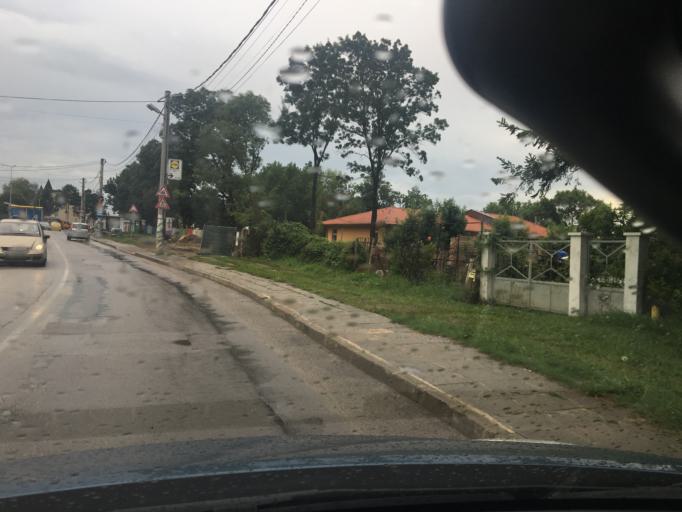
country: BG
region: Sofia-Capital
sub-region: Stolichna Obshtina
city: Sofia
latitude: 42.6302
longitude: 23.3155
